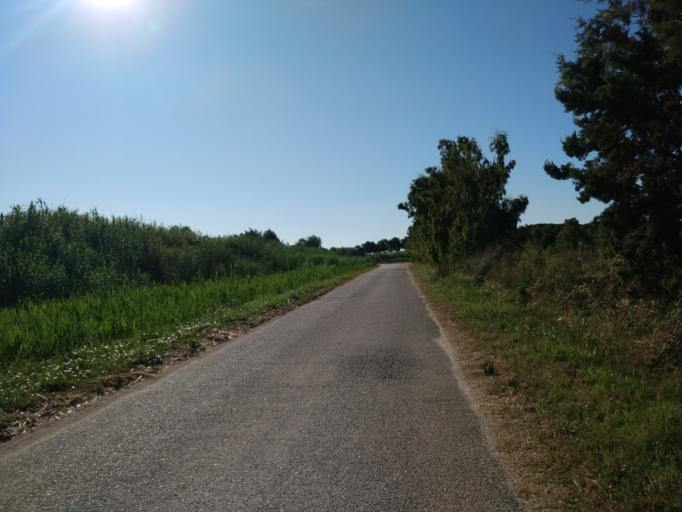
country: IT
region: Sardinia
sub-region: Provincia di Ogliastra
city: Lotzorai
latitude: 39.9601
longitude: 9.6808
